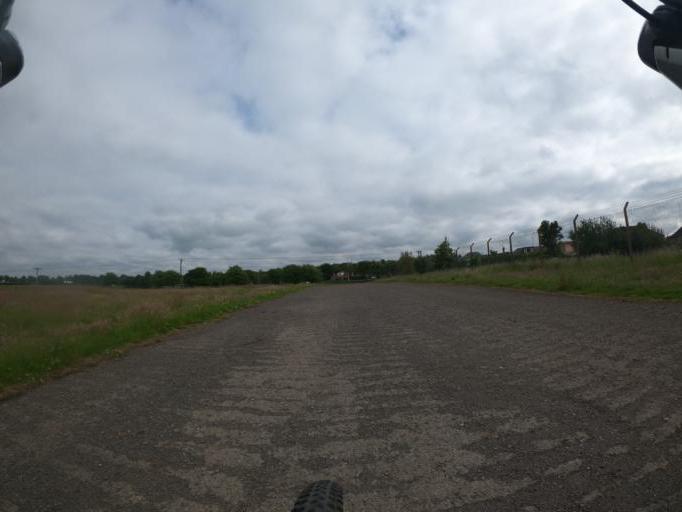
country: GB
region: Scotland
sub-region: Edinburgh
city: Newbridge
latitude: 55.9397
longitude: -3.3890
